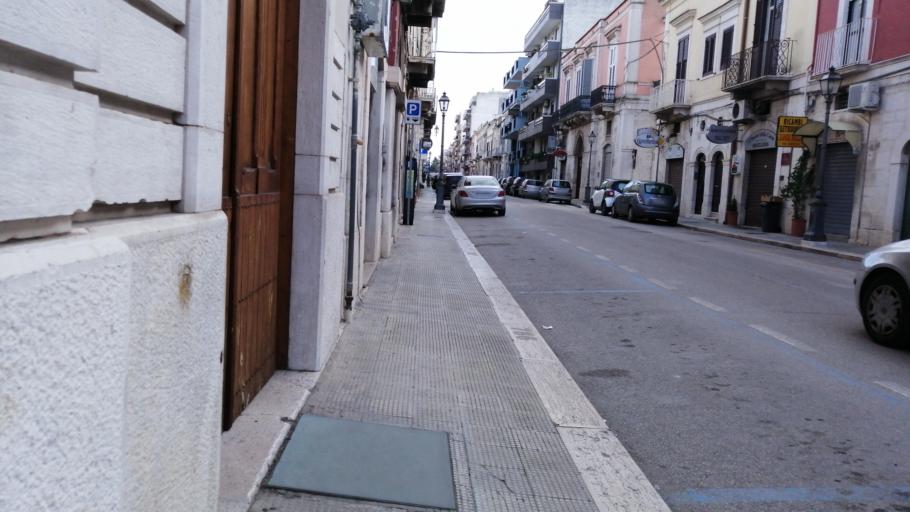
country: IT
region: Apulia
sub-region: Provincia di Barletta - Andria - Trani
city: Andria
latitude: 41.2230
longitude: 16.3008
